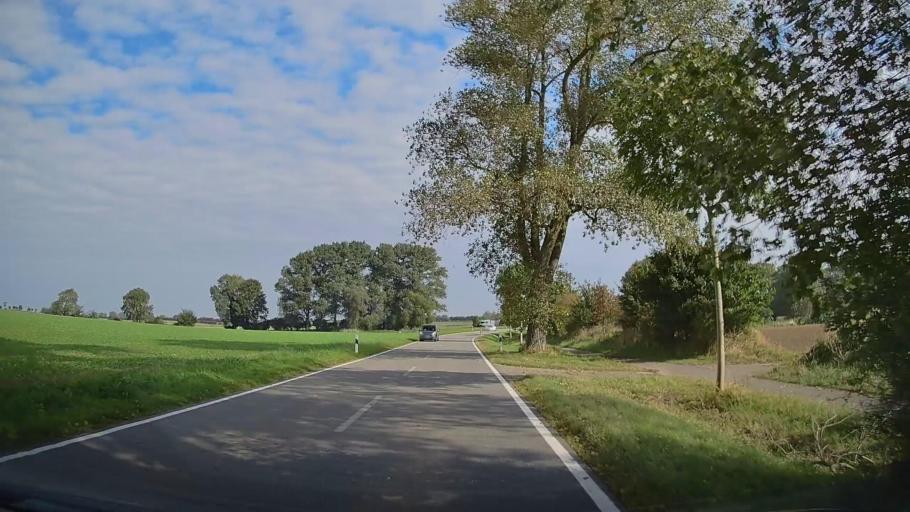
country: DE
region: Schleswig-Holstein
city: Gremersdorf
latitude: 54.3424
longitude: 10.8951
